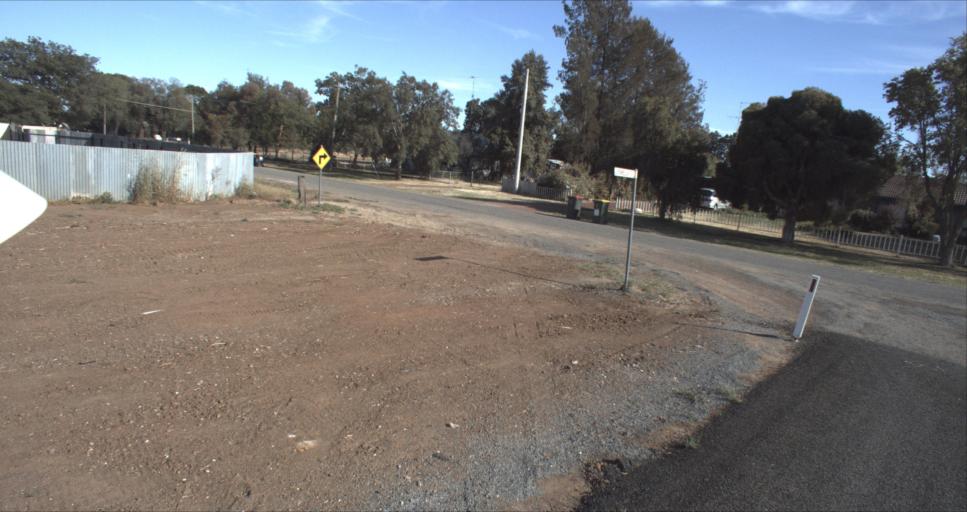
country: AU
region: New South Wales
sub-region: Leeton
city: Leeton
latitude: -34.5940
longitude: 146.4073
